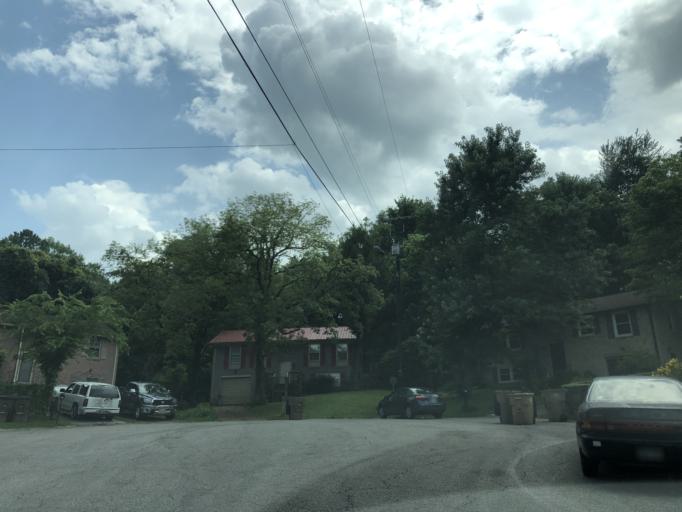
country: US
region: Tennessee
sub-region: Williamson County
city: Brentwood Estates
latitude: 36.0594
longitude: -86.6875
